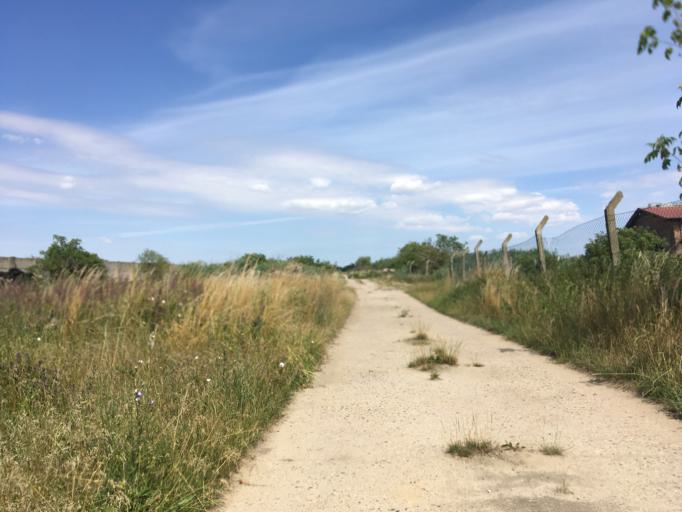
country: DE
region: Brandenburg
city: Casekow
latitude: 53.2227
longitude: 14.1394
